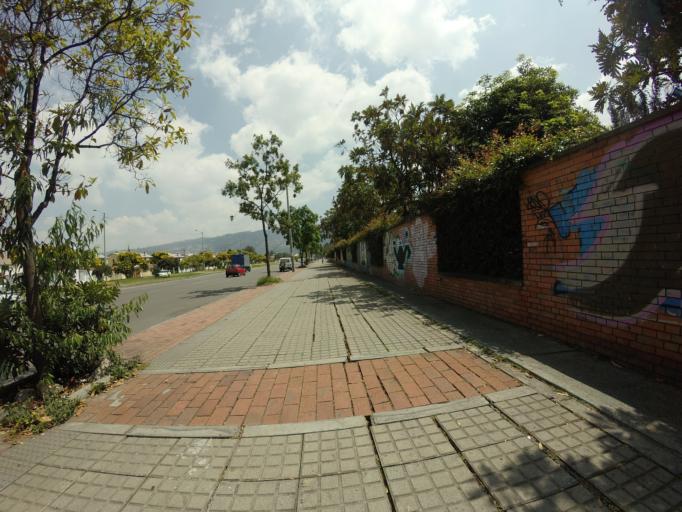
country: CO
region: Bogota D.C.
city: Barrio San Luis
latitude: 4.7371
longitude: -74.0466
